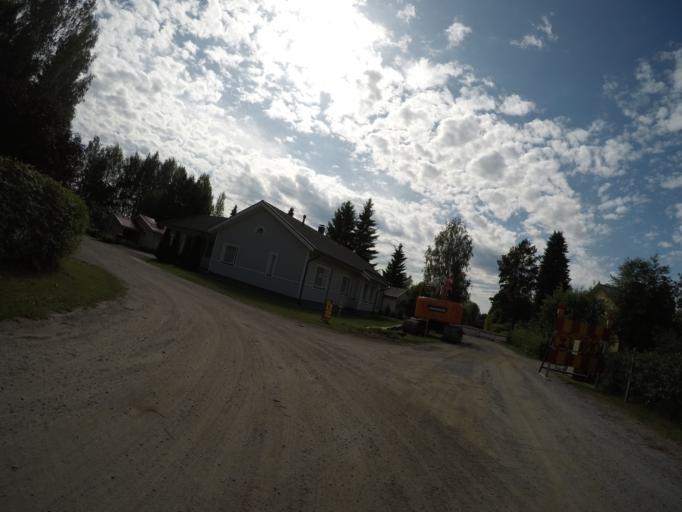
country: FI
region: Haeme
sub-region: Haemeenlinna
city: Haemeenlinna
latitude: 60.9856
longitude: 24.4044
